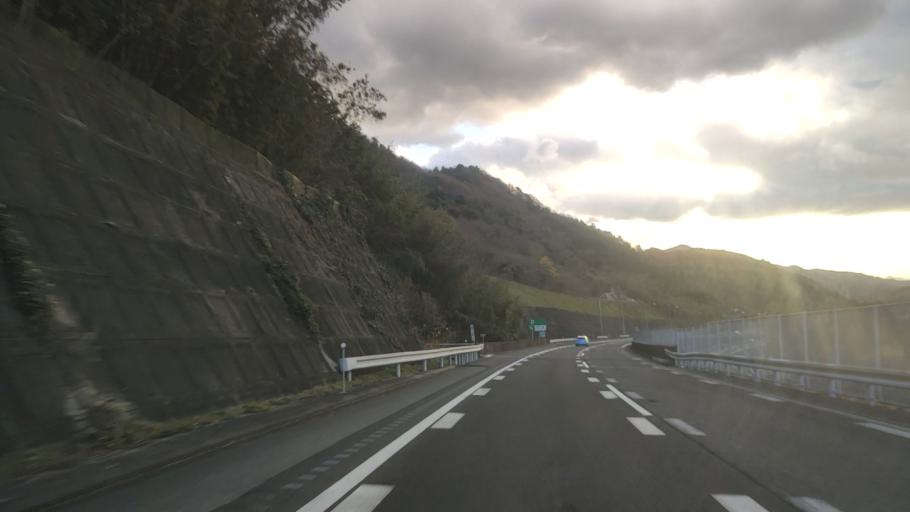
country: JP
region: Ehime
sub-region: Shikoku-chuo Shi
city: Matsuyama
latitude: 33.8053
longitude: 132.9436
